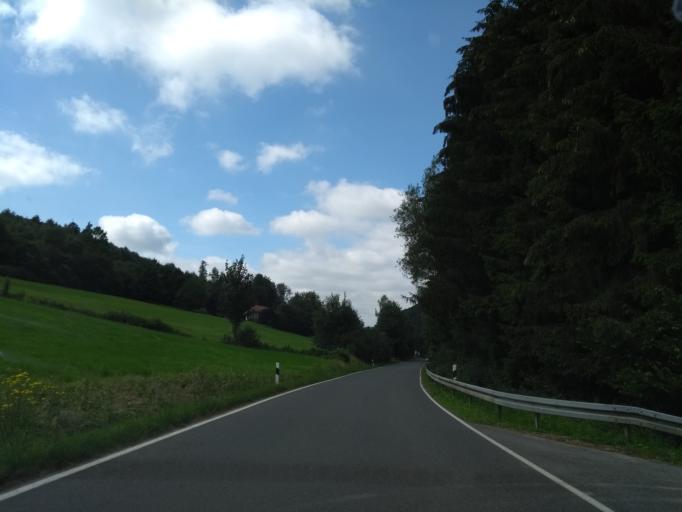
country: DE
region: North Rhine-Westphalia
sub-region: Regierungsbezirk Detmold
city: Lugde
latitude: 51.9529
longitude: 9.2648
